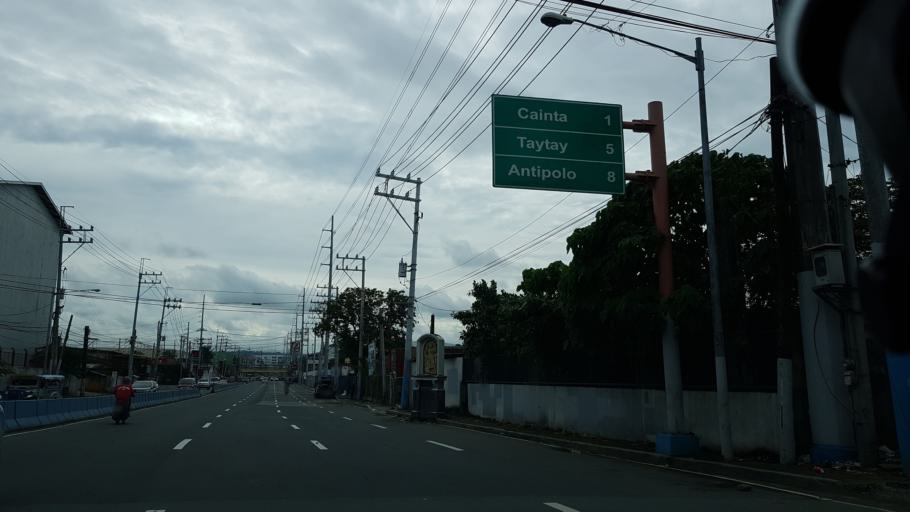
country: PH
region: Calabarzon
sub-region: Province of Rizal
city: Cainta
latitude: 14.5875
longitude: 121.1093
